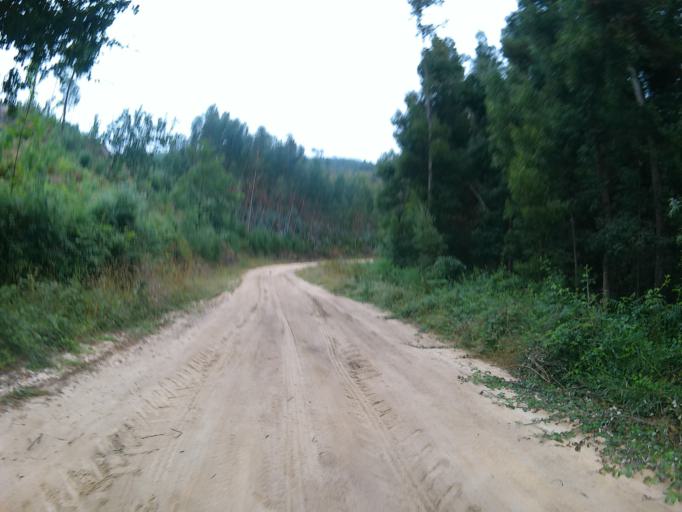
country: PT
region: Viana do Castelo
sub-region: Ponte de Lima
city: Ponte de Lima
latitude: 41.7179
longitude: -8.6111
